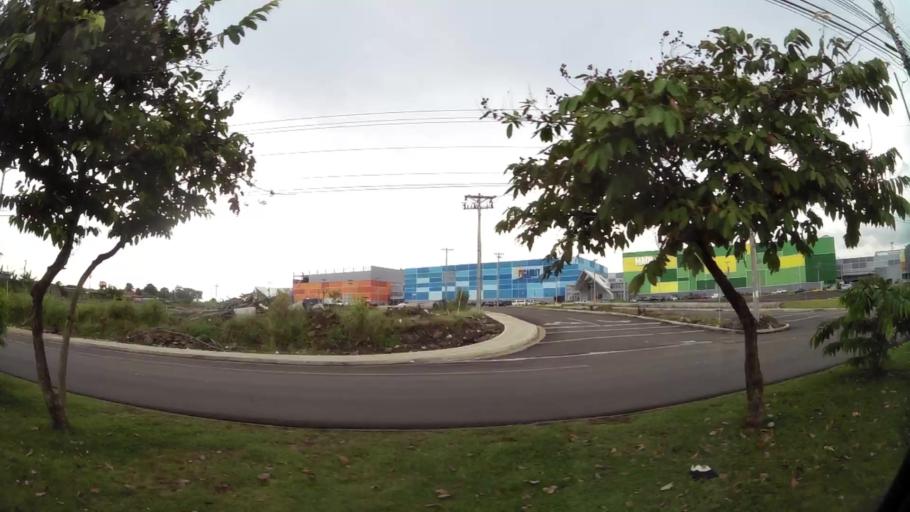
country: PA
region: Panama
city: Cabra Numero Uno
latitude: 9.0984
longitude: -79.3495
